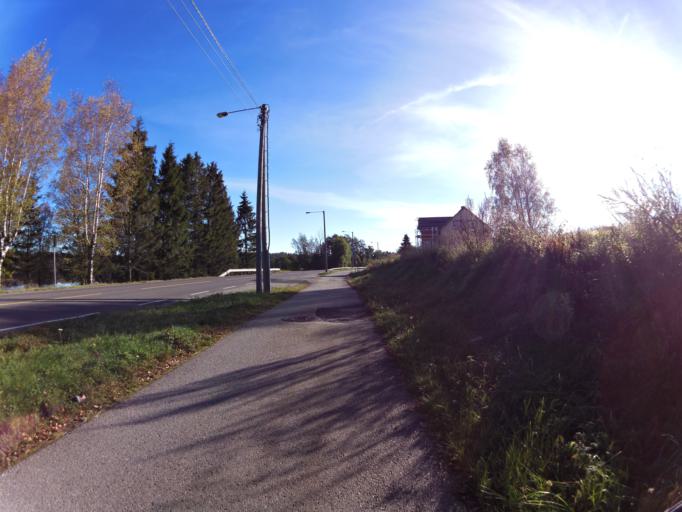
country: NO
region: Ostfold
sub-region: Fredrikstad
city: Fredrikstad
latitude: 59.2897
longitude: 11.0024
